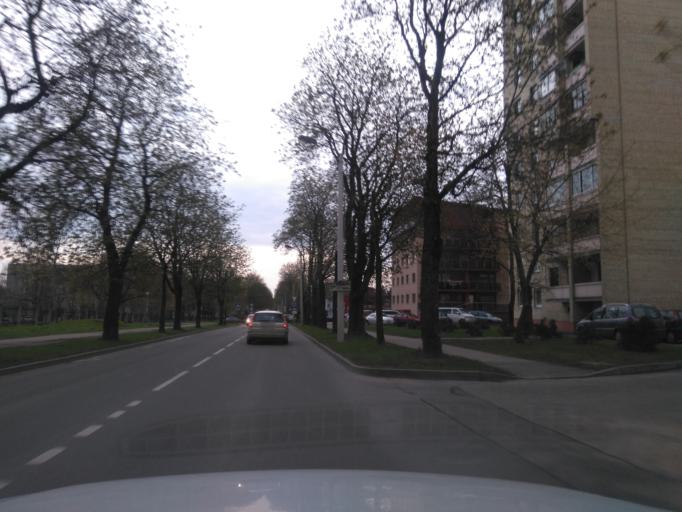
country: LT
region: Kauno apskritis
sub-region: Kaunas
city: Eiguliai
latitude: 54.9093
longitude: 23.9417
